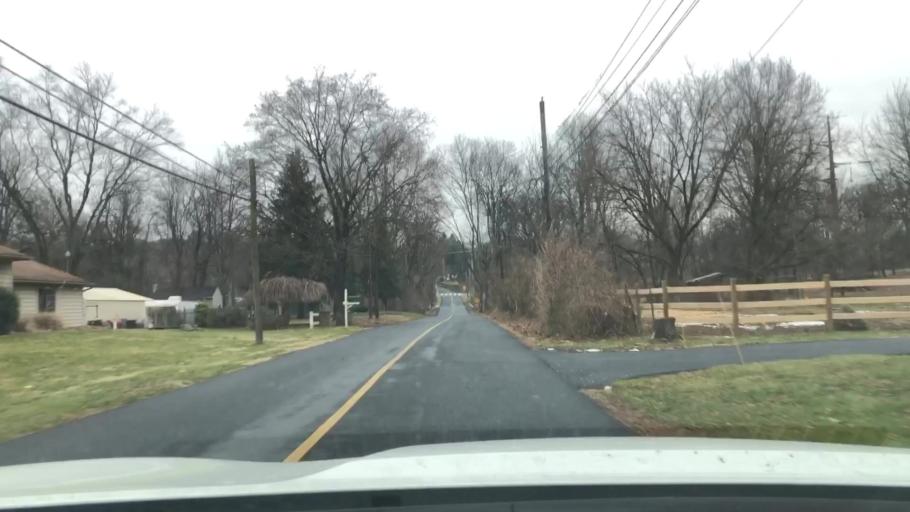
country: US
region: Pennsylvania
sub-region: Chester County
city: Spring City
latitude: 40.1969
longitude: -75.5791
